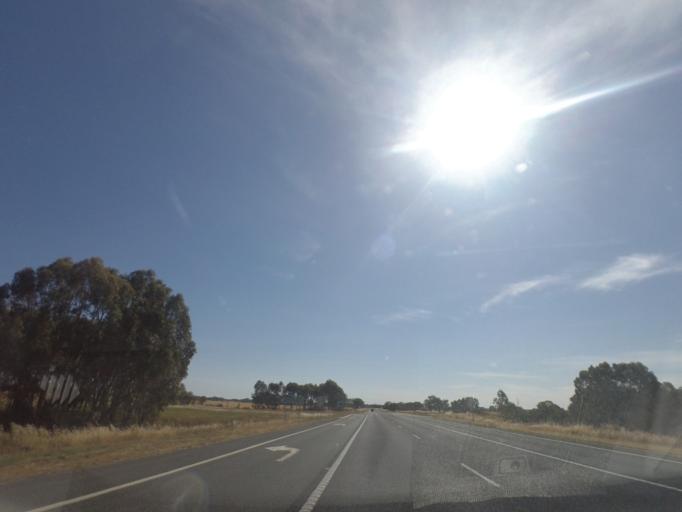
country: AU
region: Victoria
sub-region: Greater Shepparton
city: Shepparton
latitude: -36.6731
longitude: 145.2592
